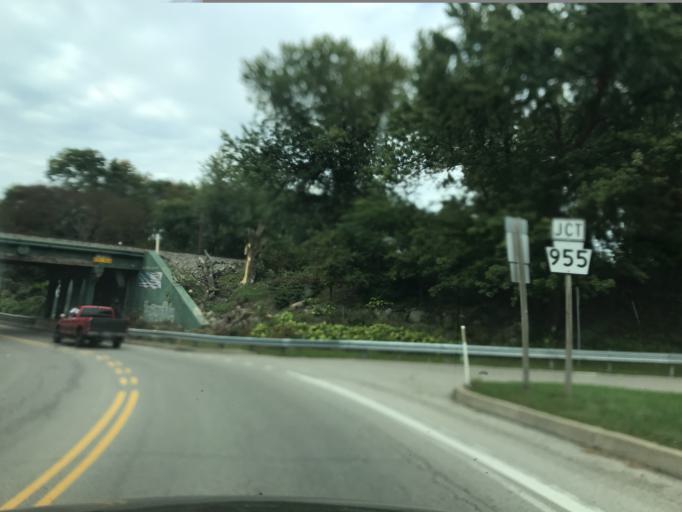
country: US
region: Pennsylvania
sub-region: Erie County
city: Northwest Harborcreek
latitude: 42.1663
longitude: -79.9529
